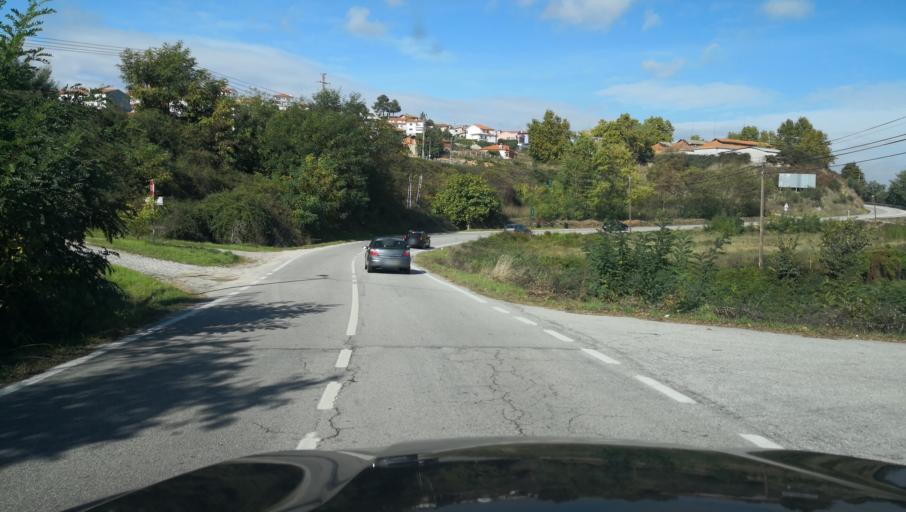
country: PT
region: Vila Real
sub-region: Chaves
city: Chaves
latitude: 41.7290
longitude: -7.4785
